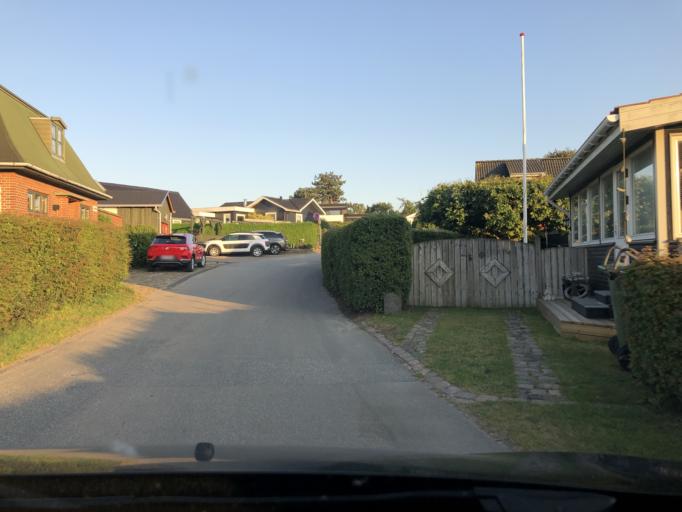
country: DK
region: South Denmark
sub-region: Vejle Kommune
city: Brejning
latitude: 55.6452
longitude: 9.7426
